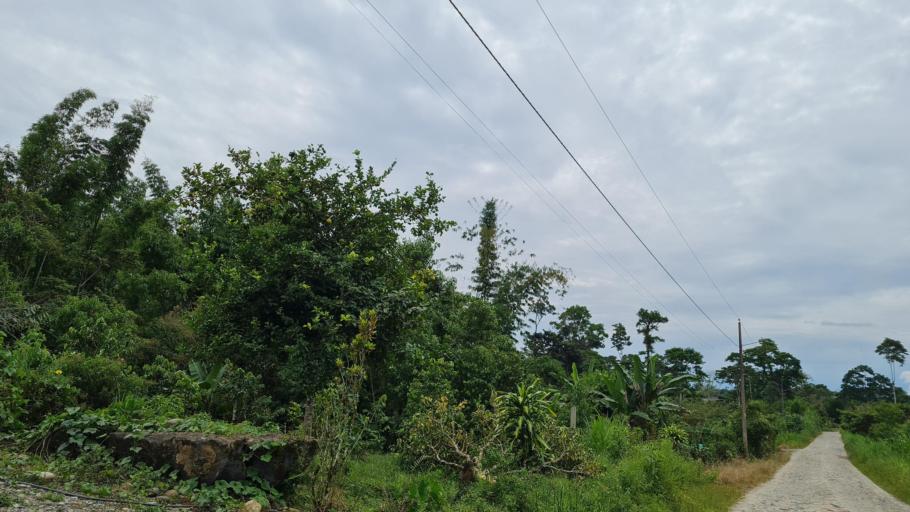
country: EC
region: Napo
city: Tena
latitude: -1.0023
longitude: -77.7676
